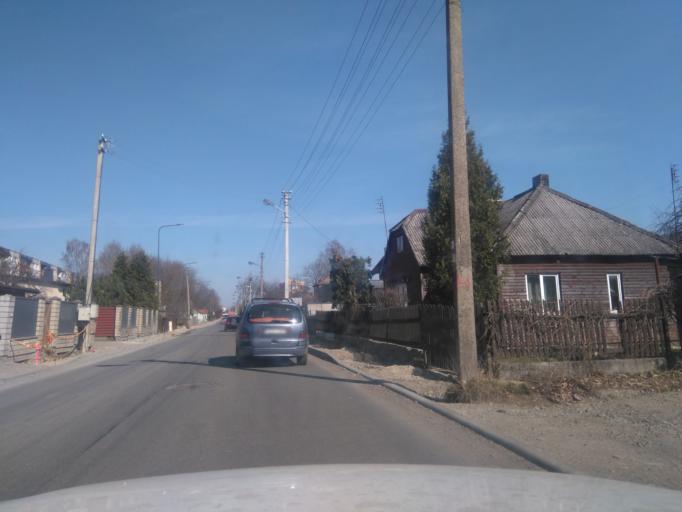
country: LT
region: Kauno apskritis
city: Dainava (Kaunas)
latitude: 54.8883
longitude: 23.9544
